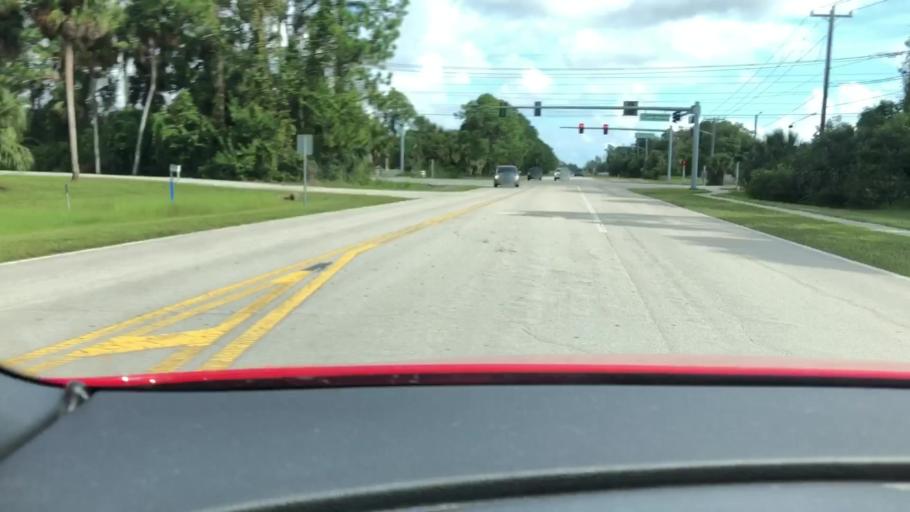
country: US
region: Florida
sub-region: Volusia County
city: Daytona Beach
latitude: 29.1951
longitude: -81.0642
